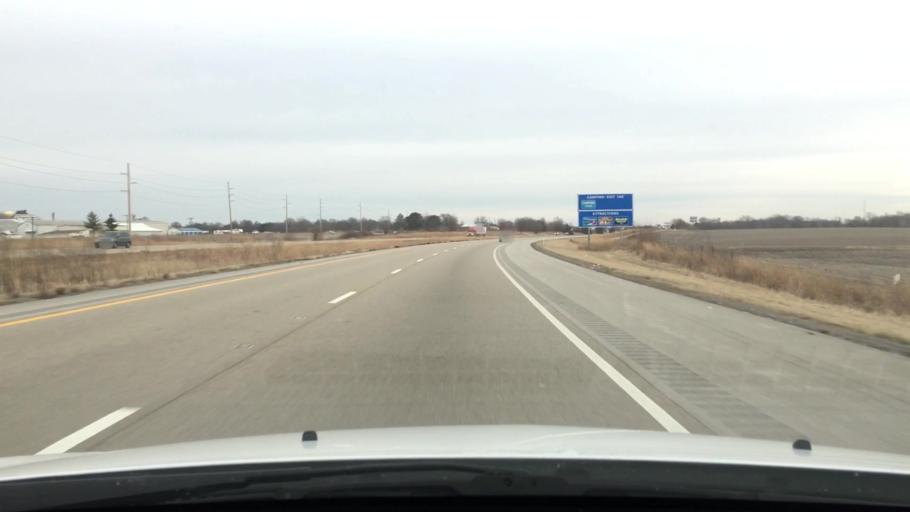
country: US
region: Illinois
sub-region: Logan County
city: Atlanta
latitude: 40.2489
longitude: -89.2439
